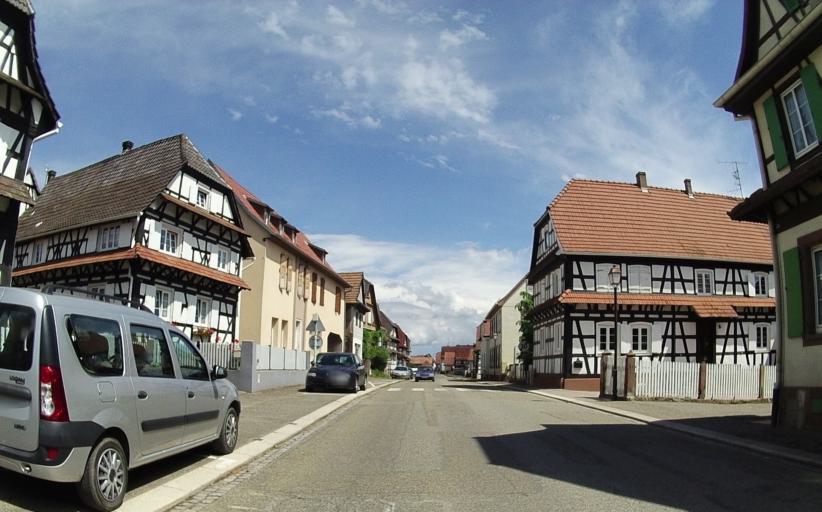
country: FR
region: Alsace
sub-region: Departement du Bas-Rhin
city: Betschdorf
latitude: 48.8987
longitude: 7.9176
